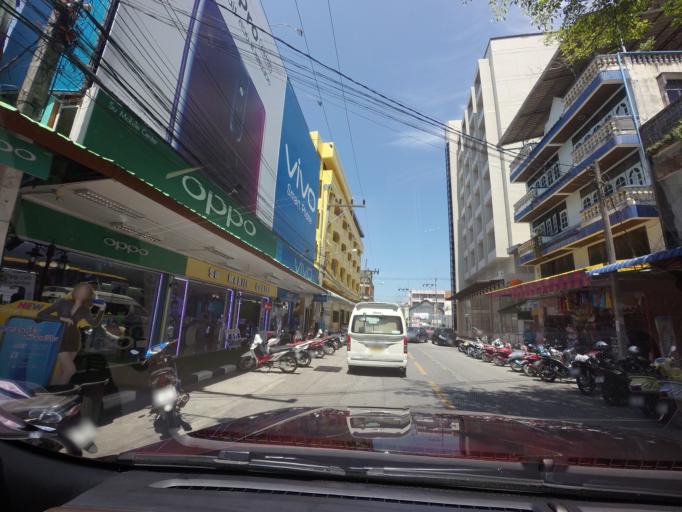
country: TH
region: Yala
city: Yala
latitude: 6.5590
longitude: 101.2931
